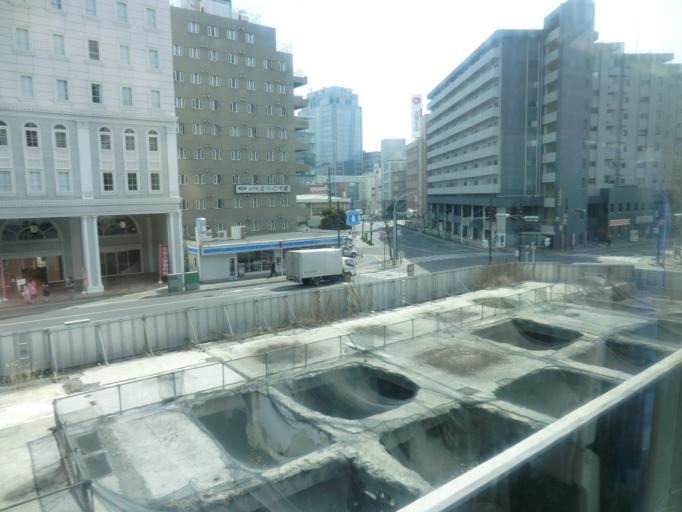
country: JP
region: Chiba
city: Chiba
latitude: 35.6060
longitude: 140.1189
